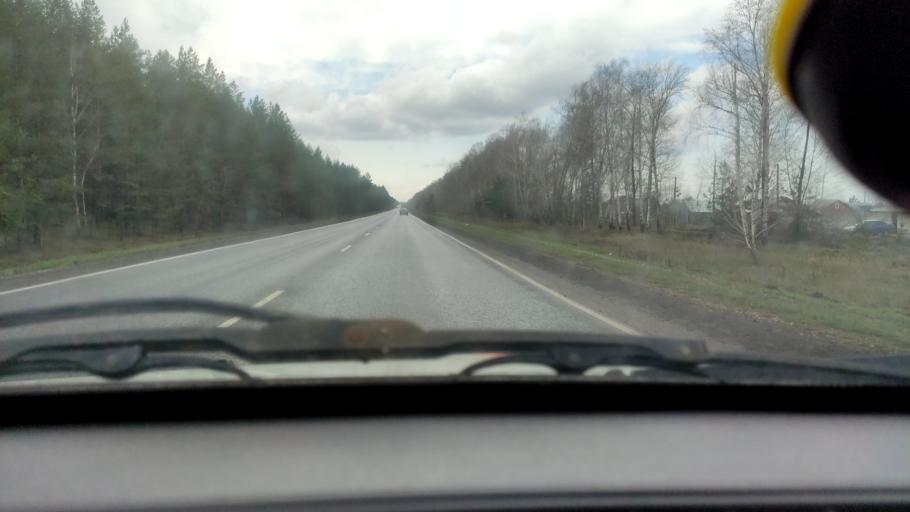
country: RU
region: Samara
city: Povolzhskiy
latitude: 53.6159
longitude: 49.6296
